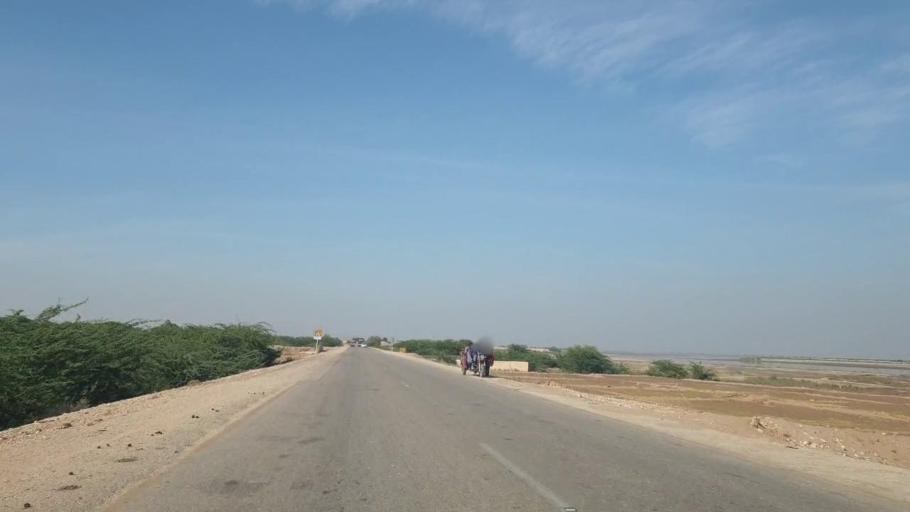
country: PK
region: Sindh
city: Sehwan
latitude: 26.3786
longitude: 67.8725
